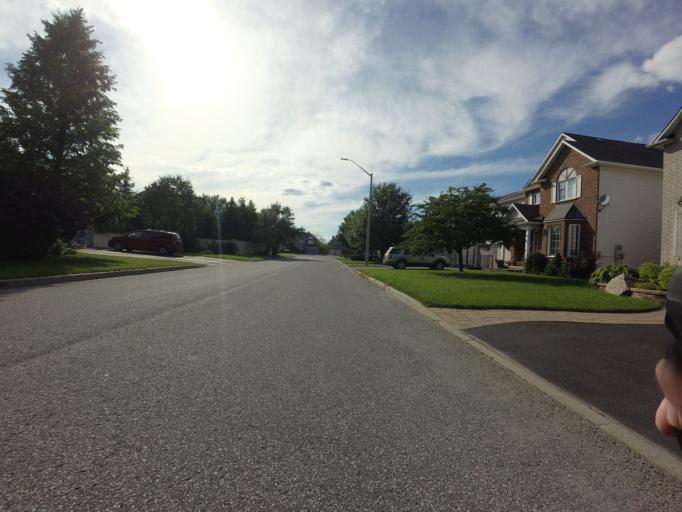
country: CA
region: Ontario
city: Ottawa
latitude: 45.2883
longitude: -75.6902
